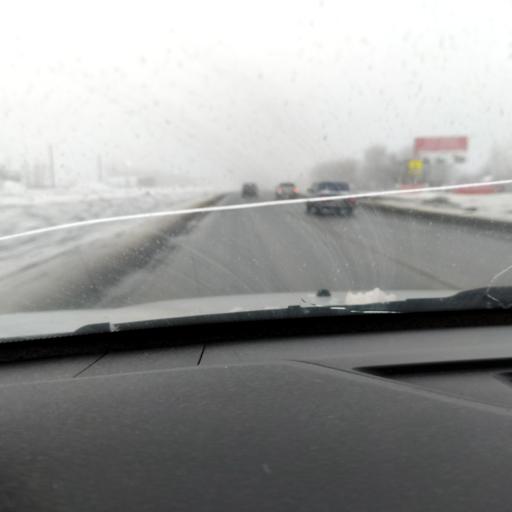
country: RU
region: Samara
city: Smyshlyayevka
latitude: 53.2596
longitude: 50.4448
